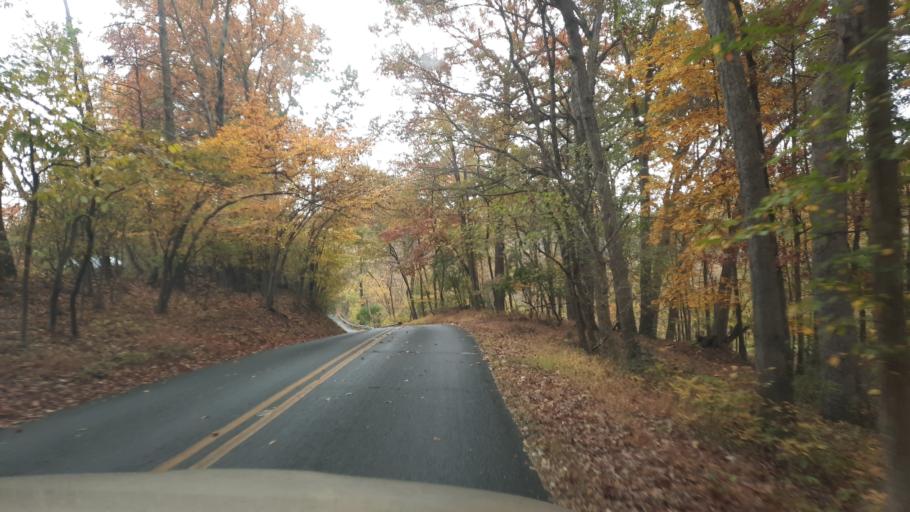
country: US
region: Maryland
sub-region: Montgomery County
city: Gaithersburg
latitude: 39.1639
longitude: -77.2289
